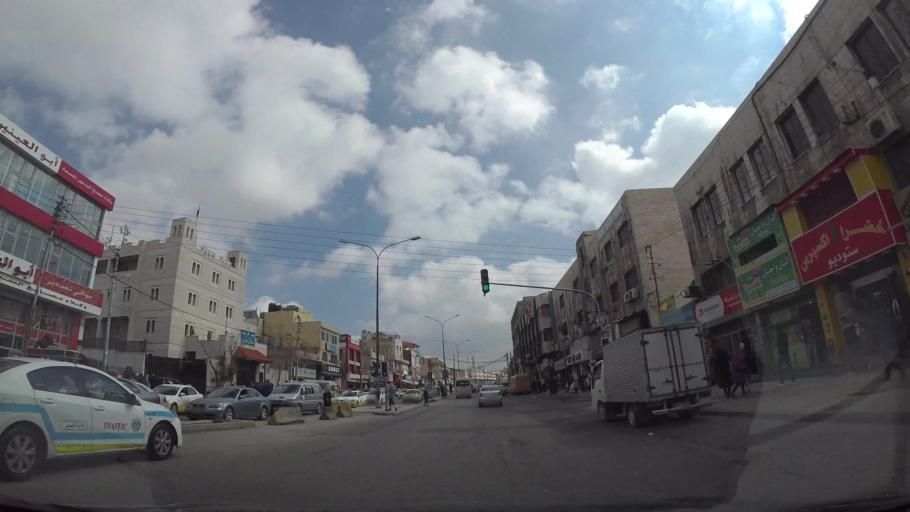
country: JO
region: Amman
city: Al Quwaysimah
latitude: 31.9310
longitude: 35.9354
